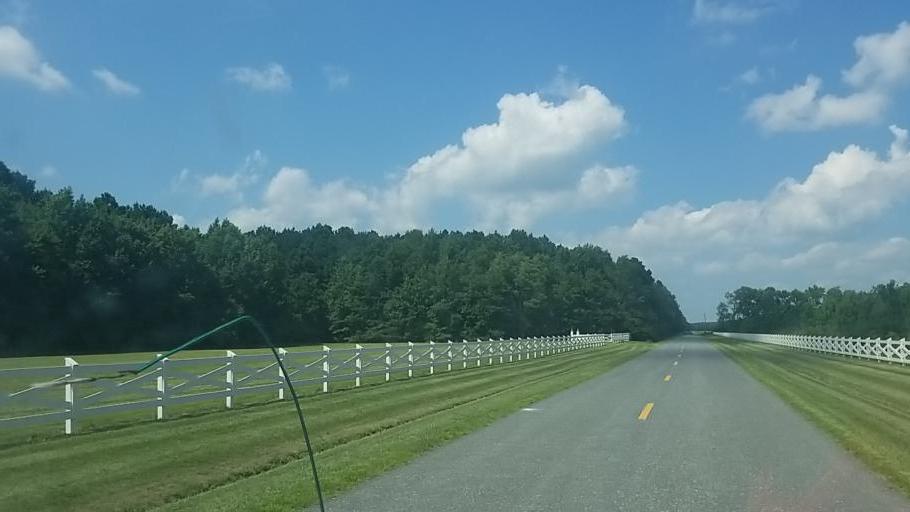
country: US
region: Maryland
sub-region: Wicomico County
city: Hebron
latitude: 38.4532
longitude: -75.8484
